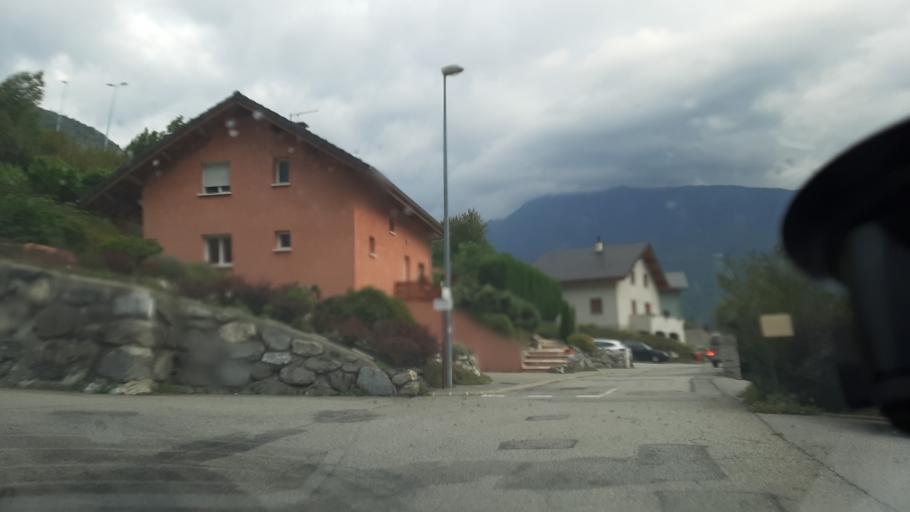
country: FR
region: Rhone-Alpes
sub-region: Departement de la Savoie
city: Saint-Michel-de-Maurienne
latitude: 45.2292
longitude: 6.4617
